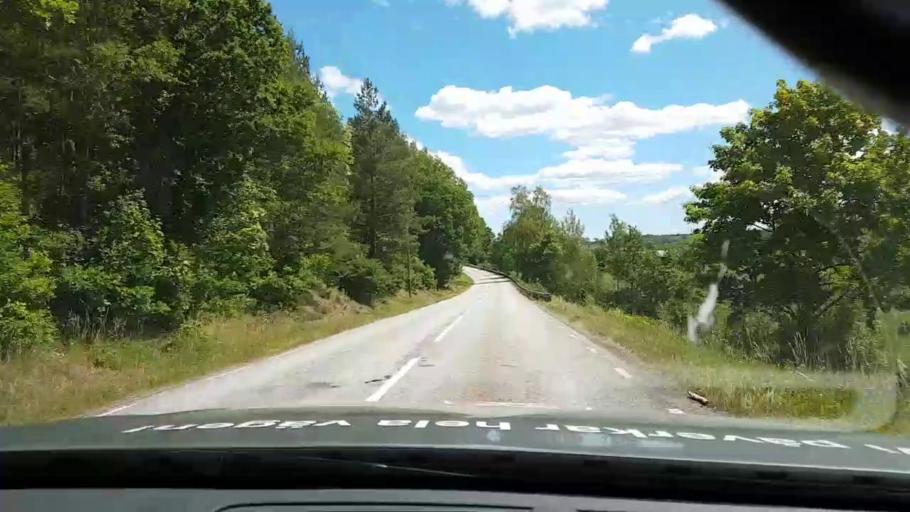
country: SE
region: Kalmar
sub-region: Vasterviks Kommun
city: Overum
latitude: 58.0756
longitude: 16.3621
